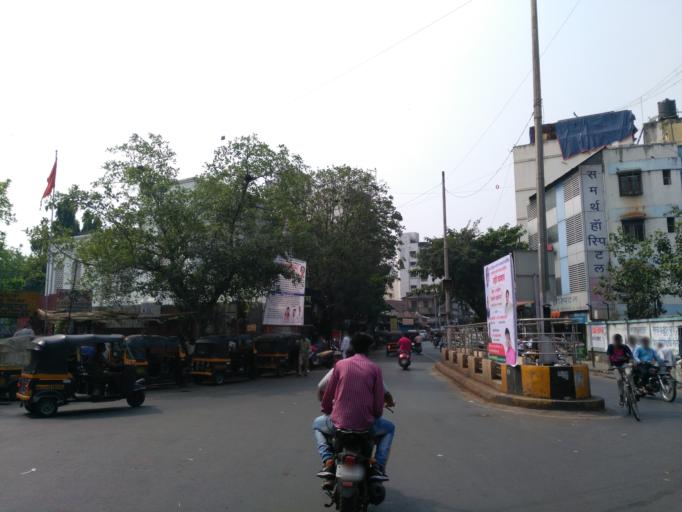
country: IN
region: Maharashtra
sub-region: Pune Division
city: Pune
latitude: 18.5196
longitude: 73.8624
